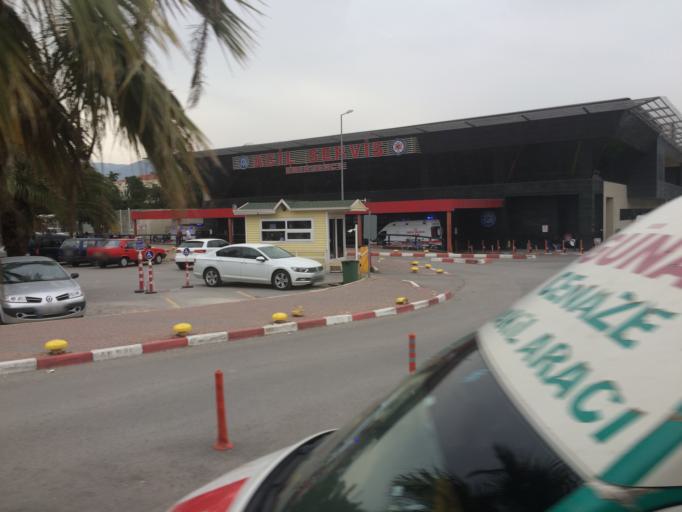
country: TR
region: Izmir
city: Bornova
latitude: 38.4575
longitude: 27.2091
